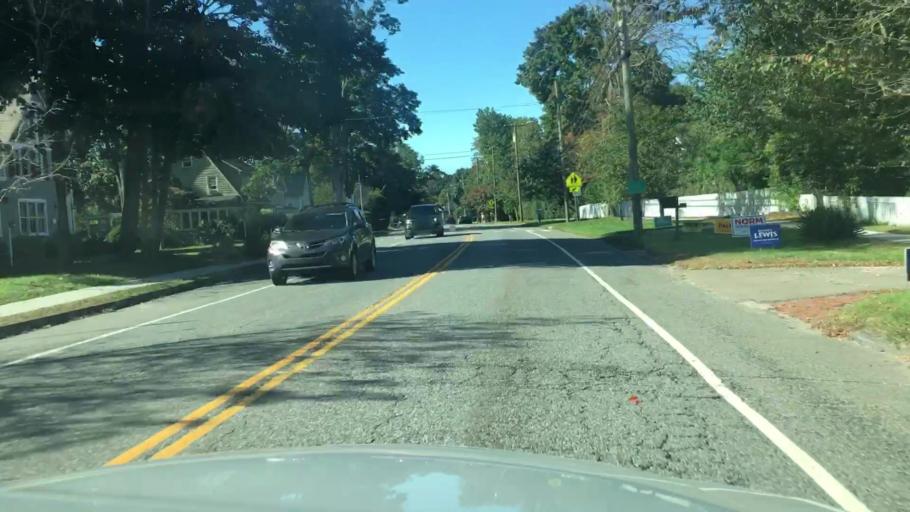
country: US
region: Connecticut
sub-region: Middlesex County
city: Essex Village
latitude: 41.3505
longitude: -72.4206
